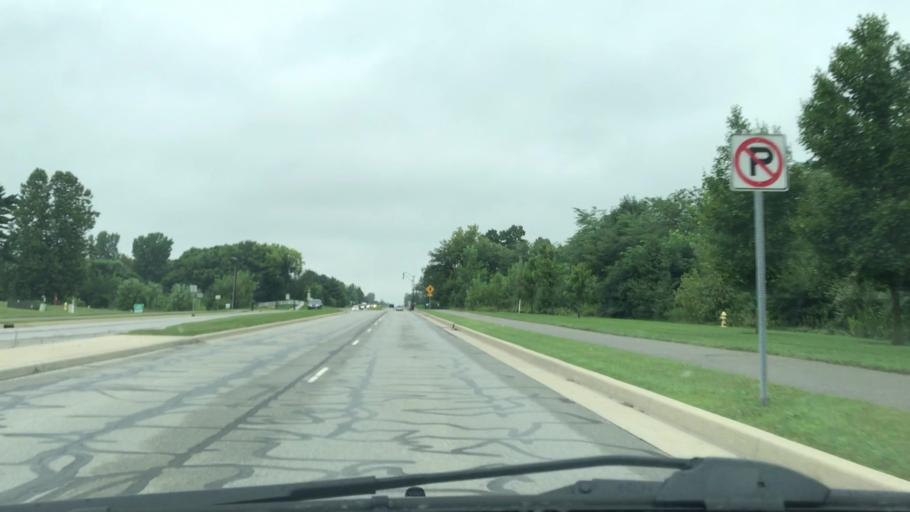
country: US
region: Indiana
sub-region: Hamilton County
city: Carmel
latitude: 40.0124
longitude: -86.0705
